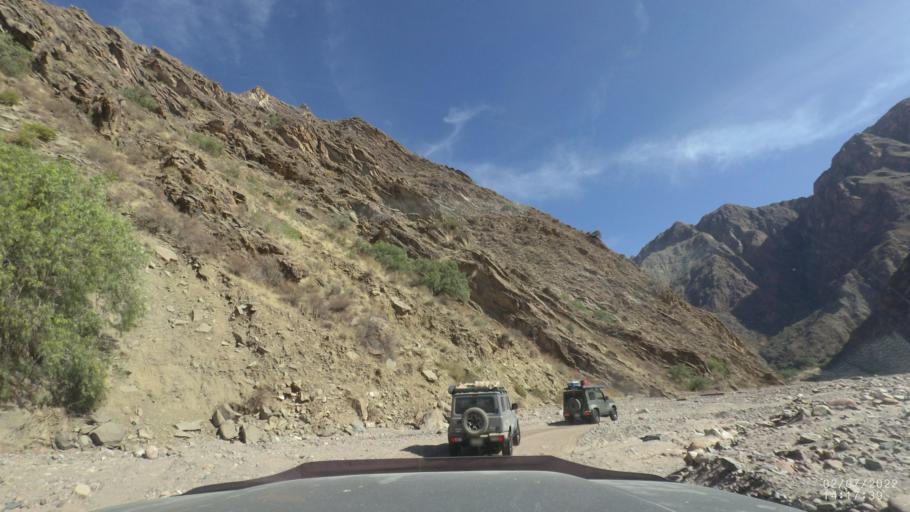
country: BO
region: Cochabamba
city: Irpa Irpa
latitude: -17.8271
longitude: -66.4076
